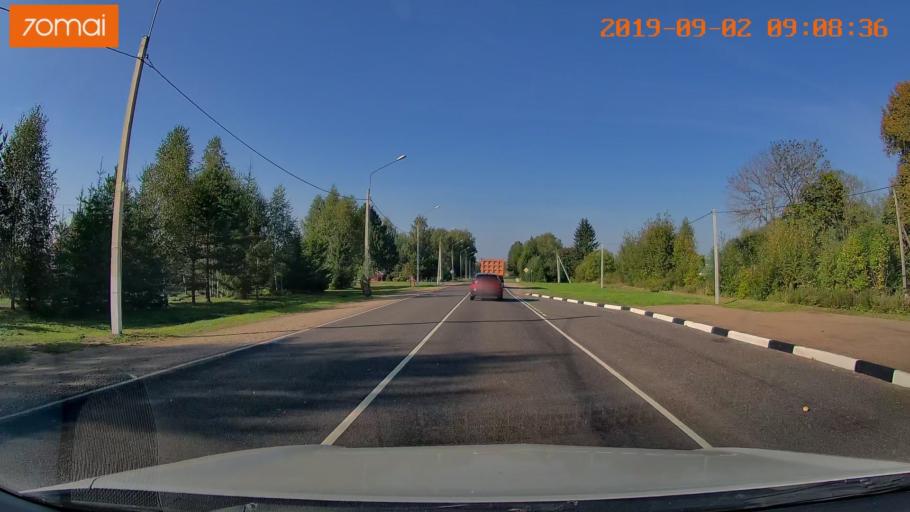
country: RU
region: Kaluga
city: Myatlevo
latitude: 54.8895
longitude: 35.6397
